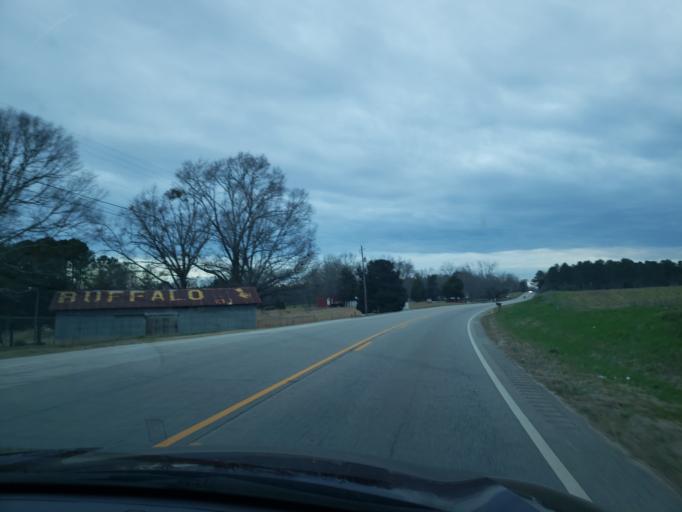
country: US
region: Alabama
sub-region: Chambers County
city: Lafayette
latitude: 32.9486
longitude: -85.4027
